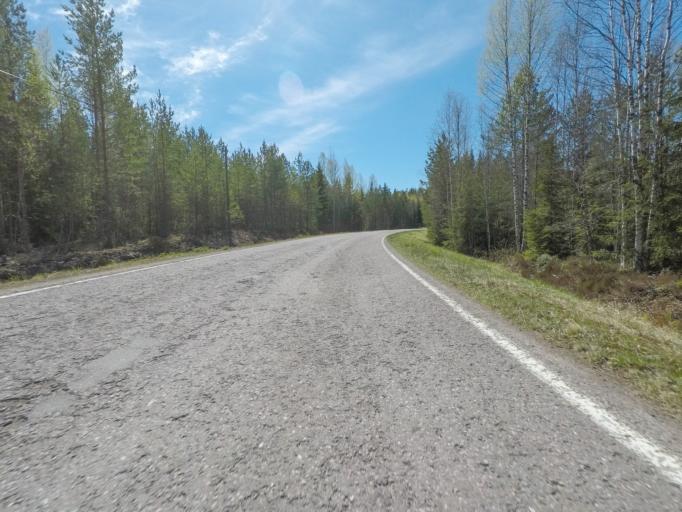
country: FI
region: Uusimaa
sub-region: Helsinki
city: Kaerkoelae
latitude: 60.6138
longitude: 23.8503
